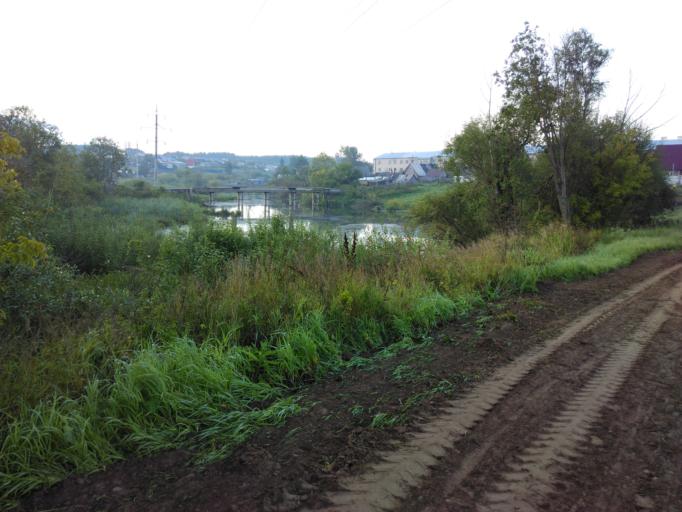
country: RU
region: Perm
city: Foki
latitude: 56.7008
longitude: 54.3563
